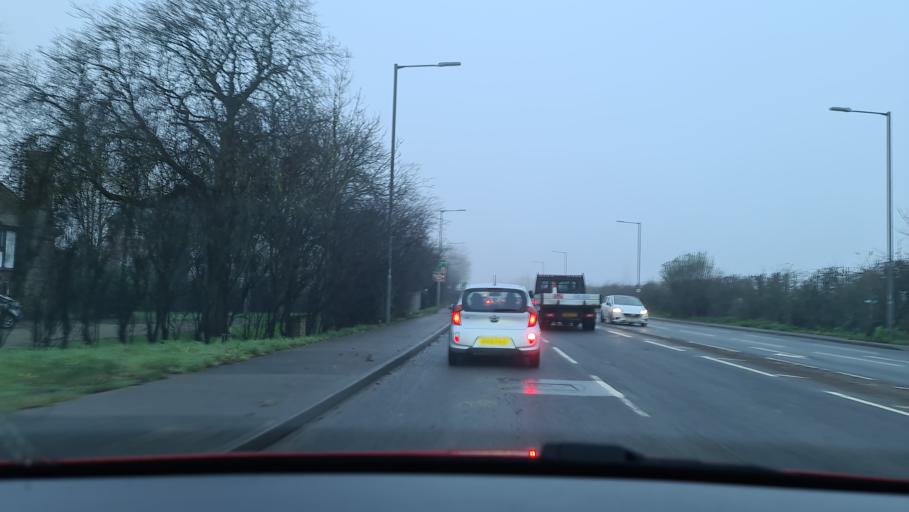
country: GB
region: England
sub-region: Buckinghamshire
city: Weston Turville
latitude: 51.8102
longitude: -0.7697
